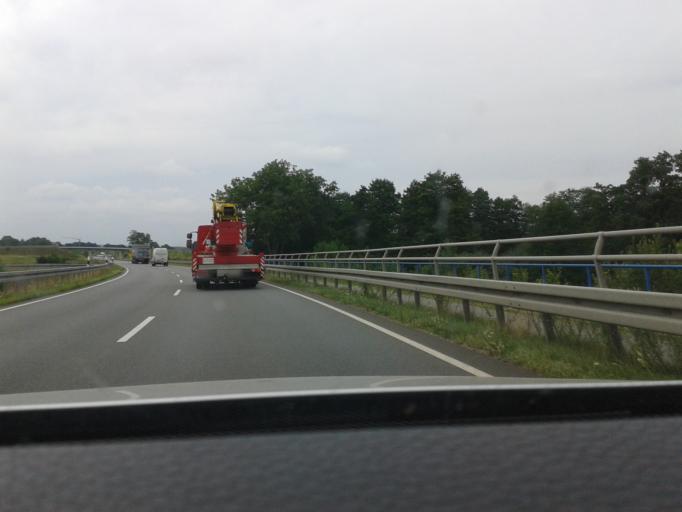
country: DE
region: Lower Saxony
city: Burgdorf
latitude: 52.4522
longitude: 10.0356
